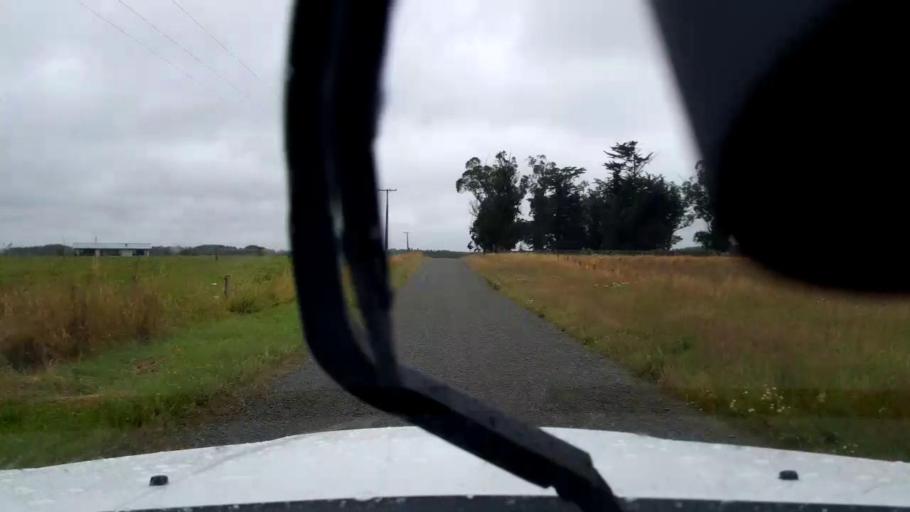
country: NZ
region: Canterbury
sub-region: Timaru District
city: Pleasant Point
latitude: -44.2496
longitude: 171.2006
